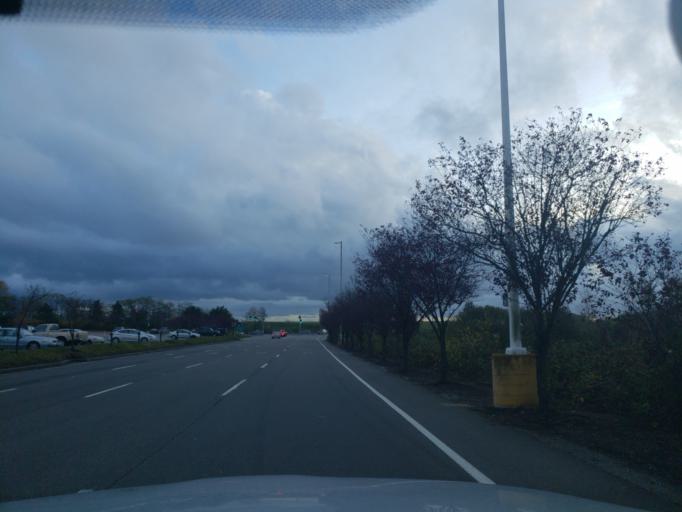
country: US
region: Washington
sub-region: Snohomish County
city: Mukilteo
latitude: 47.9264
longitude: -122.2846
